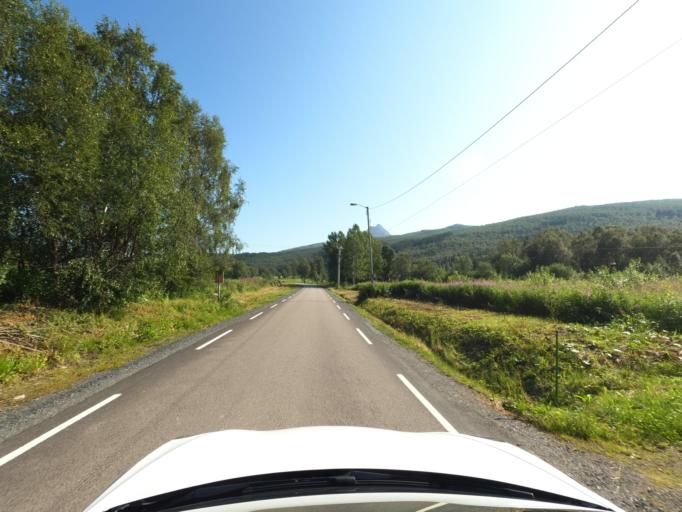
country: NO
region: Nordland
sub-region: Narvik
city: Narvik
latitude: 68.3986
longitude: 17.2955
